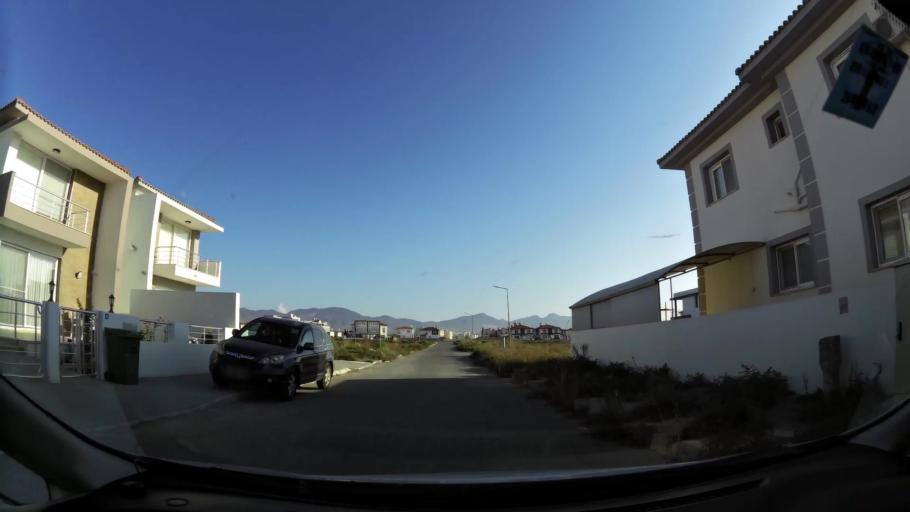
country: CY
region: Lefkosia
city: Nicosia
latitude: 35.2019
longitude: 33.2962
